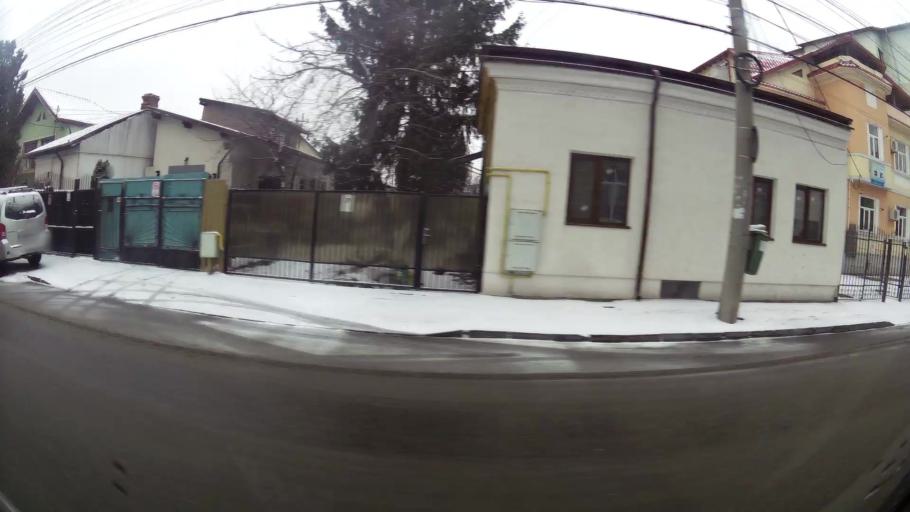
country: RO
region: Prahova
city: Ploiesti
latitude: 44.9343
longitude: 26.0207
